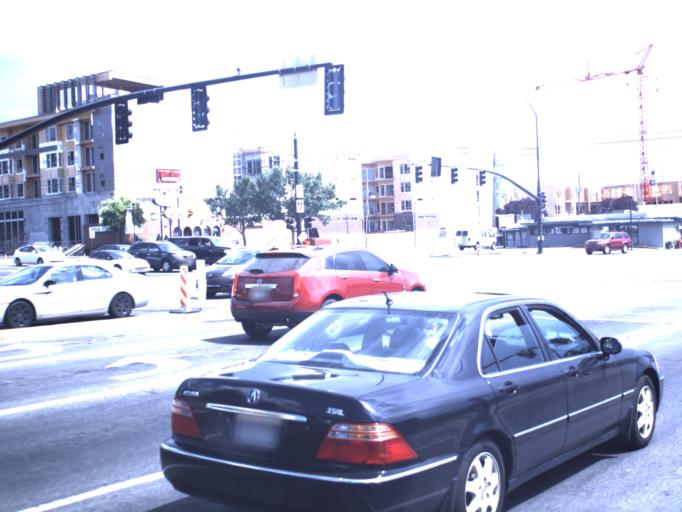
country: US
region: Utah
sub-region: Salt Lake County
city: Salt Lake City
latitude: 40.7611
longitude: -111.8712
